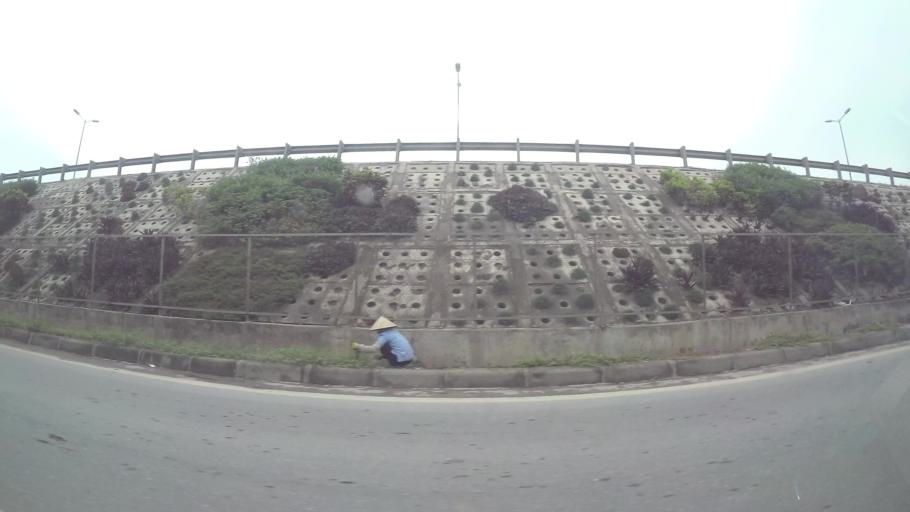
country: VN
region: Ha Noi
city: Van Dien
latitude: 20.9737
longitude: 105.8820
